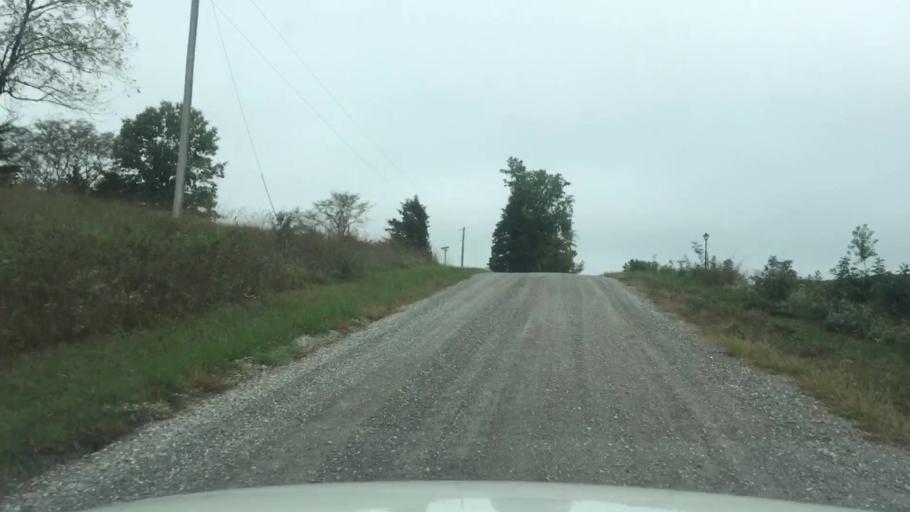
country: US
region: Missouri
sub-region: Boone County
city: Columbia
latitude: 38.8923
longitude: -92.4194
